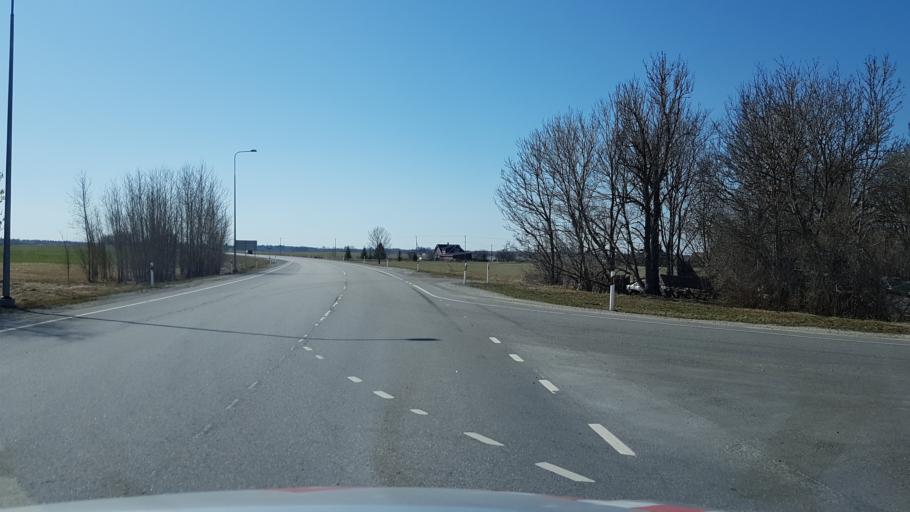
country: EE
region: Ida-Virumaa
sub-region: Kohtla-Jaerve linn
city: Kohtla-Jarve
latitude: 59.3559
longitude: 27.2401
